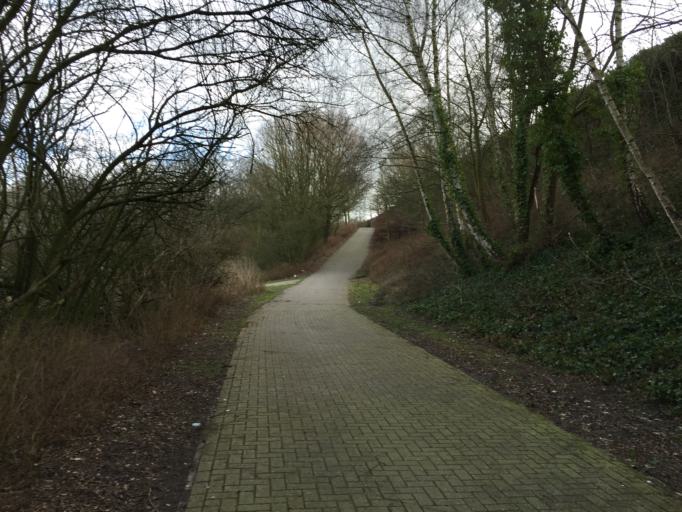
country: DE
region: Lower Saxony
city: Oldenburg
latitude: 53.1636
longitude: 8.2278
